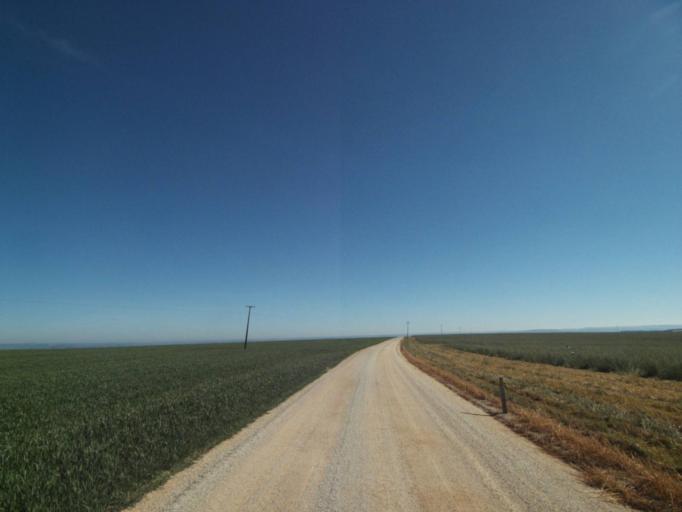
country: BR
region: Parana
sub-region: Tibagi
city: Tibagi
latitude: -24.5352
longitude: -50.3056
